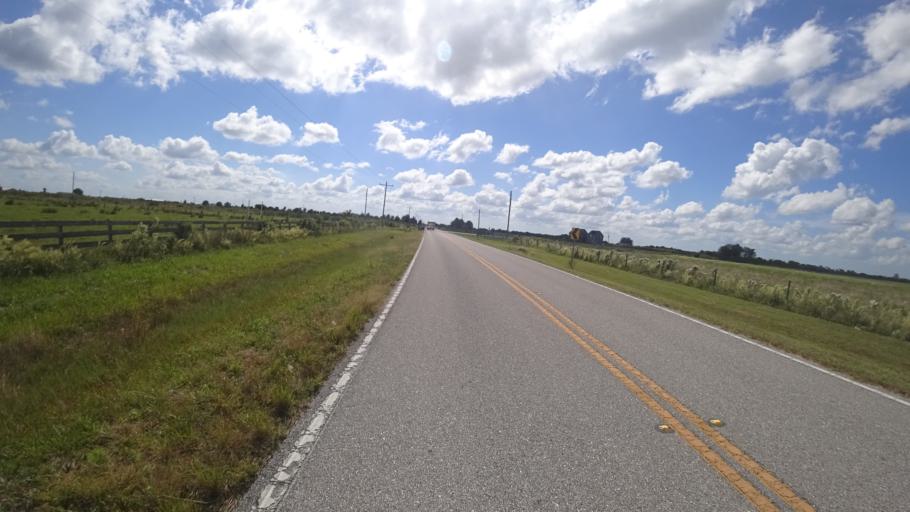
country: US
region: Florida
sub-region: Sarasota County
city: Lake Sarasota
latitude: 27.3018
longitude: -82.1878
